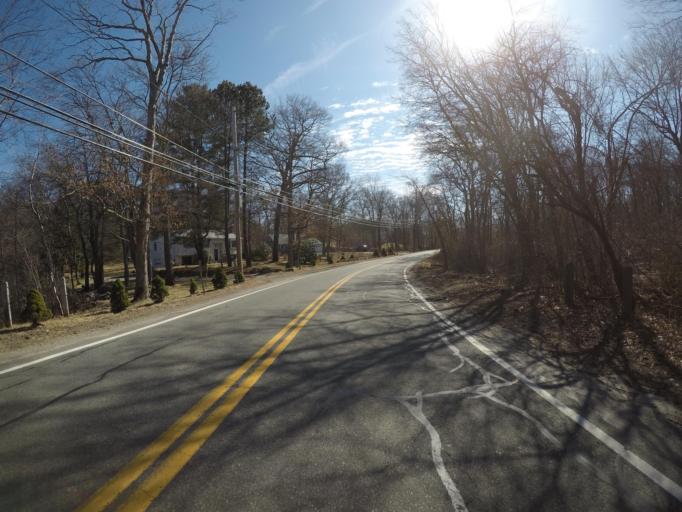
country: US
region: Massachusetts
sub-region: Norfolk County
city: Stoughton
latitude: 42.0843
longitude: -71.1391
